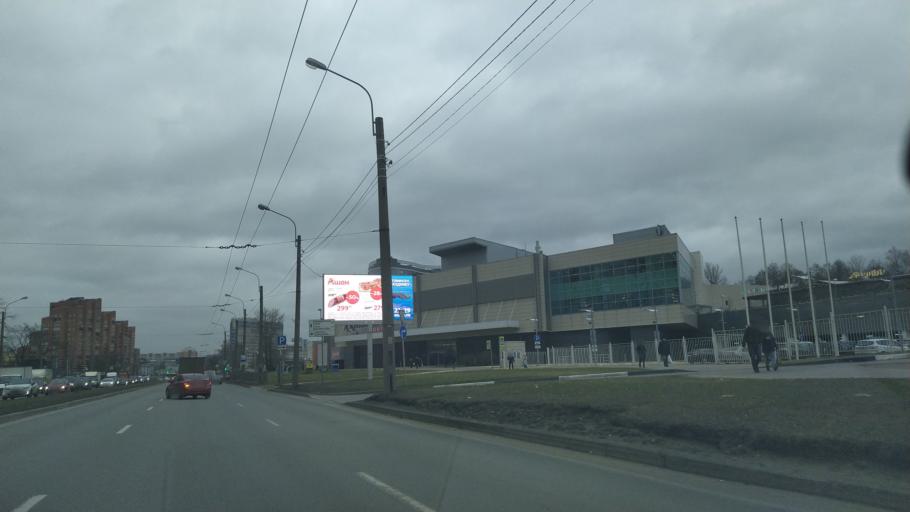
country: RU
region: St.-Petersburg
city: Kolomyagi
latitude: 60.0070
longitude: 30.2967
